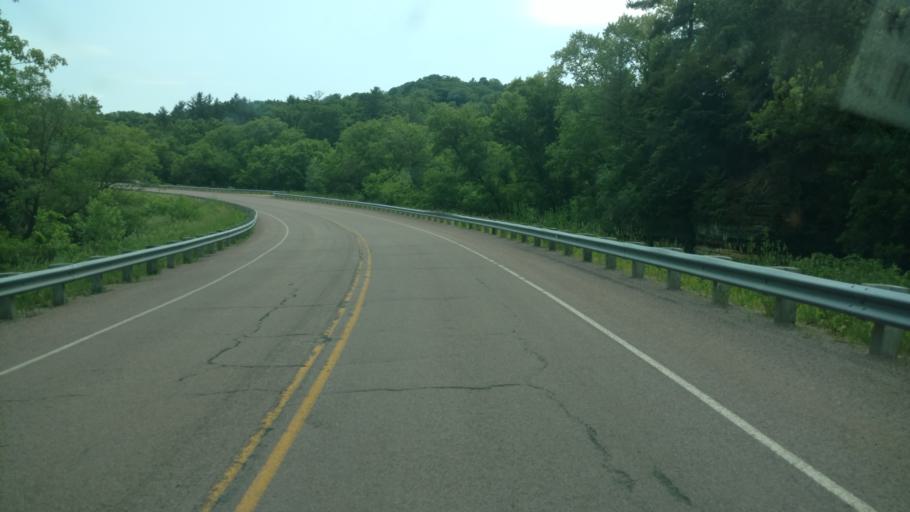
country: US
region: Wisconsin
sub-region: Monroe County
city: Cashton
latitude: 43.6741
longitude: -90.5947
